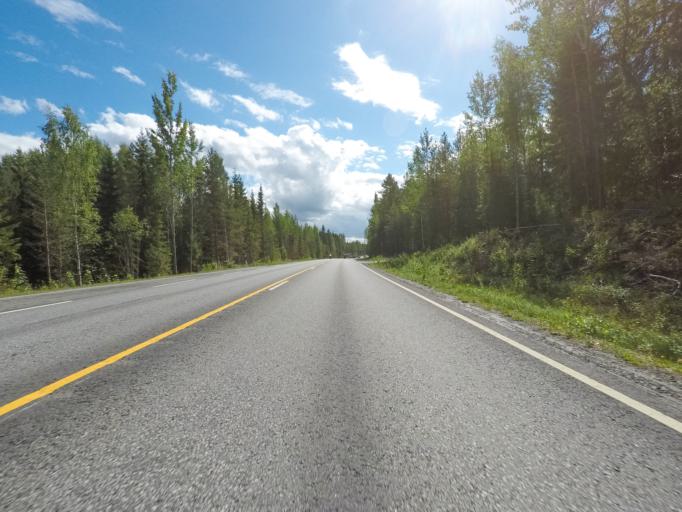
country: FI
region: Central Finland
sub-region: Jyvaeskylae
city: Toivakka
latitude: 62.2151
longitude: 26.2074
